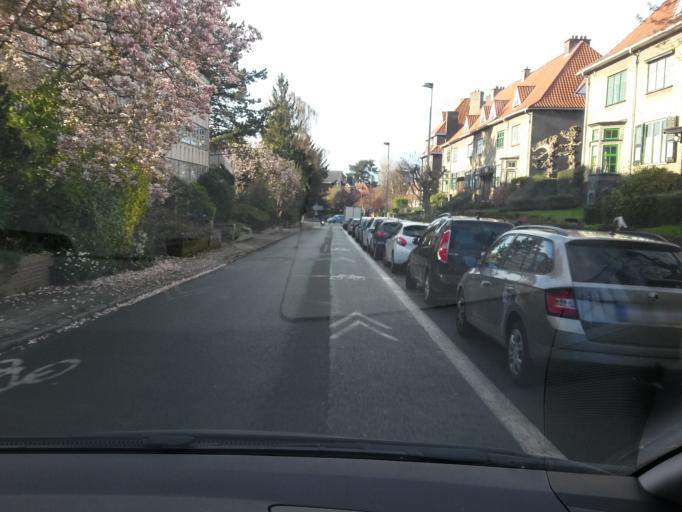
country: BE
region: Flanders
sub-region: Provincie Vlaams-Brabant
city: Hoeilaart
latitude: 50.8020
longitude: 4.4090
